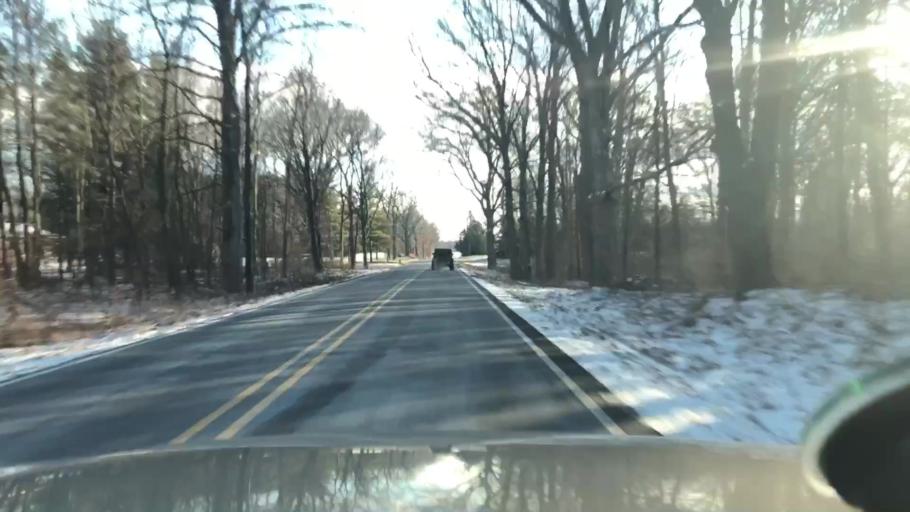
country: US
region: Michigan
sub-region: Jackson County
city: Vandercook Lake
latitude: 42.1063
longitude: -84.4512
